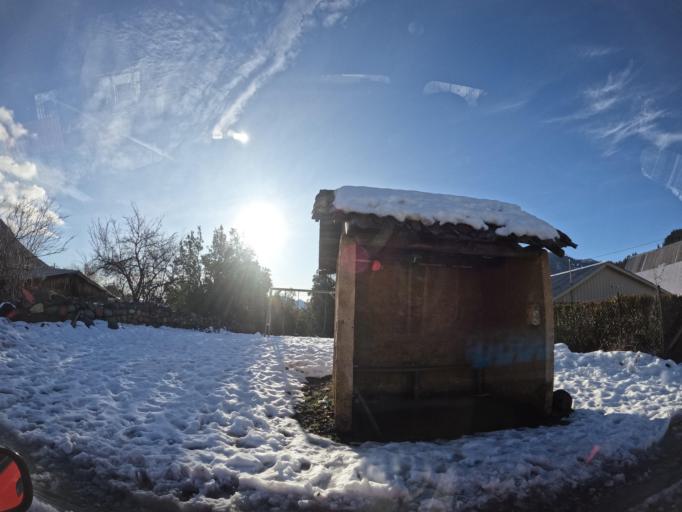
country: CL
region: Biobio
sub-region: Provincia de Nuble
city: Coihueco
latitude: -37.3702
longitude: -71.4908
